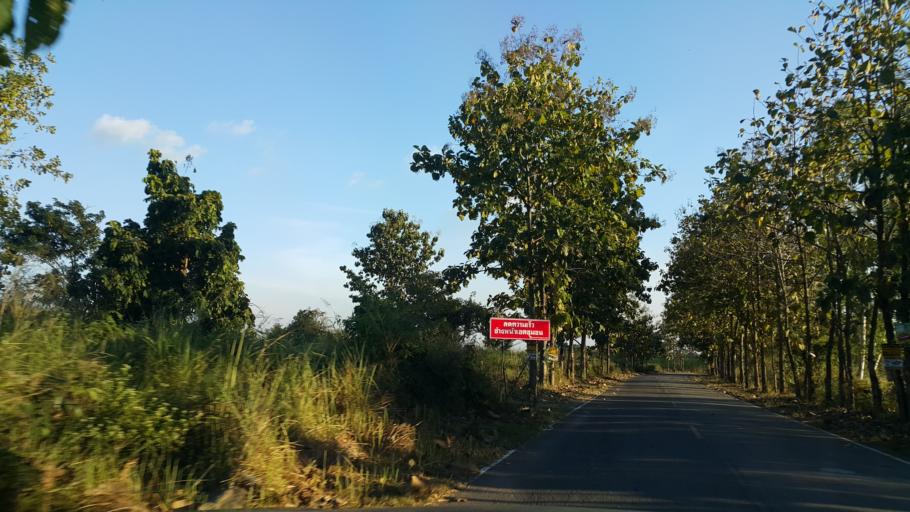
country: TH
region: Sukhothai
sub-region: Amphoe Si Satchanalai
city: Si Satchanalai
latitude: 17.5501
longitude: 99.9032
